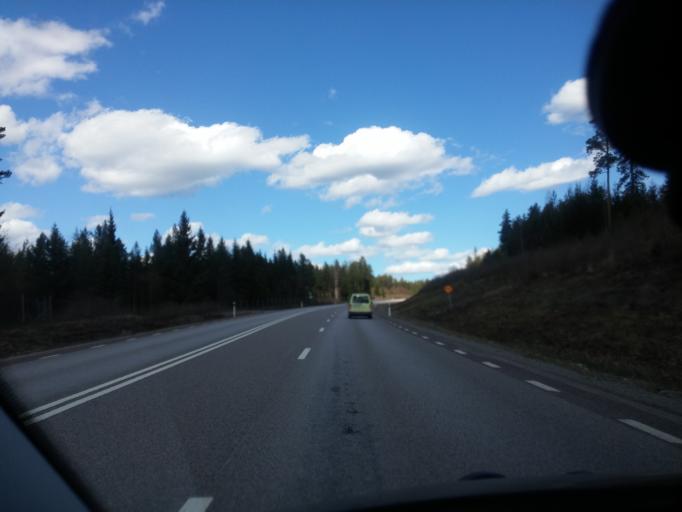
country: SE
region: Dalarna
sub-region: Faluns Kommun
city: Falun
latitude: 60.6685
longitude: 15.6467
